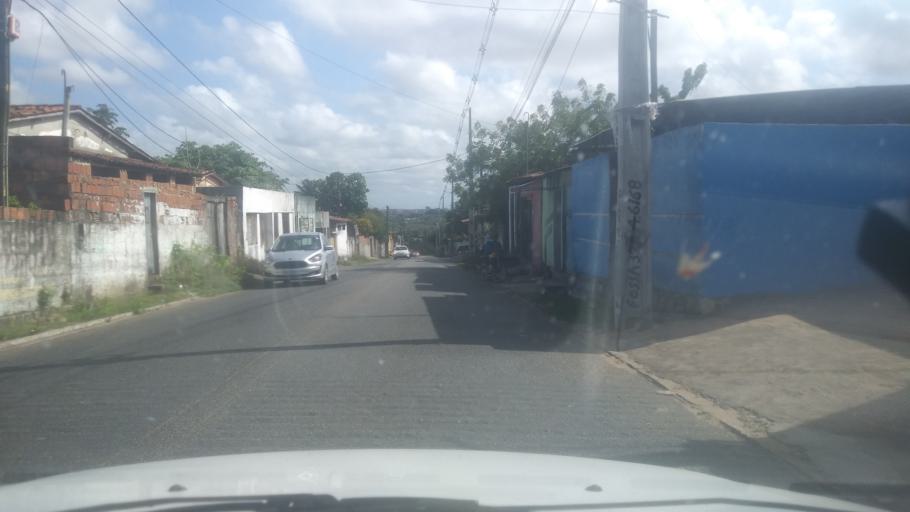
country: BR
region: Rio Grande do Norte
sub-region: Extremoz
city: Extremoz
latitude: -5.7131
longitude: -35.2776
